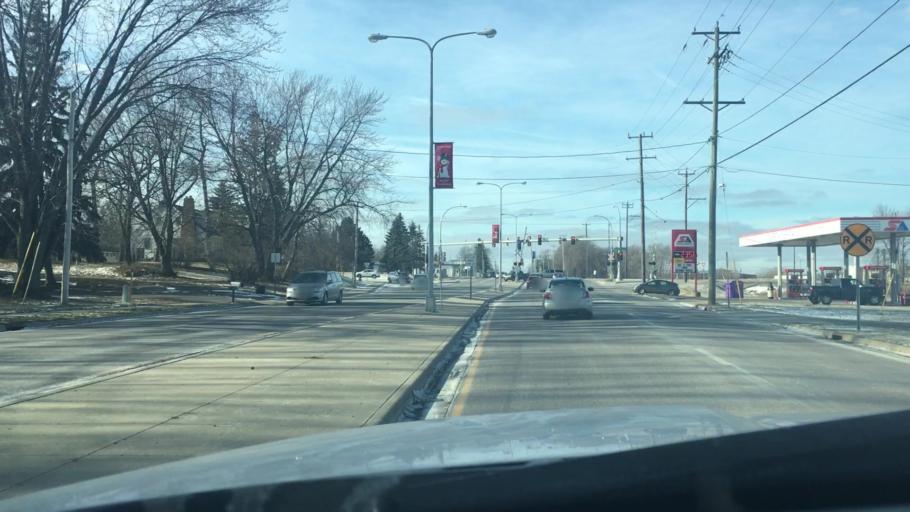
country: US
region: Minnesota
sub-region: Stearns County
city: Waite Park
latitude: 45.5589
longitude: -94.2117
